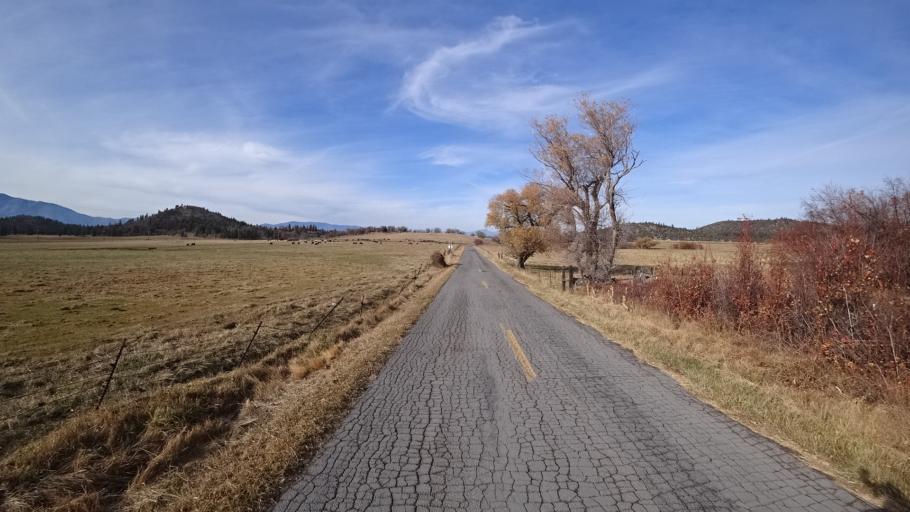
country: US
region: California
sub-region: Siskiyou County
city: Weed
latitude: 41.4504
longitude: -122.3814
